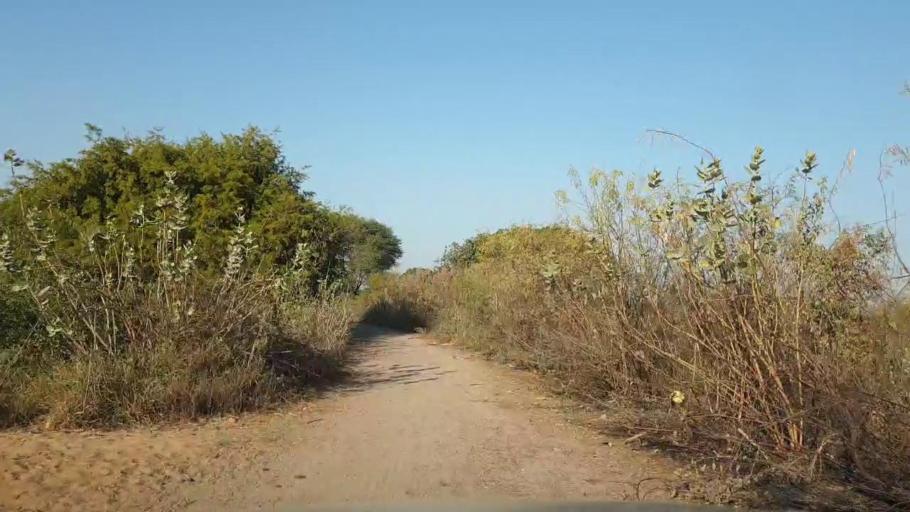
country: PK
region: Sindh
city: Tando Allahyar
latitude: 25.4855
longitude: 68.6418
